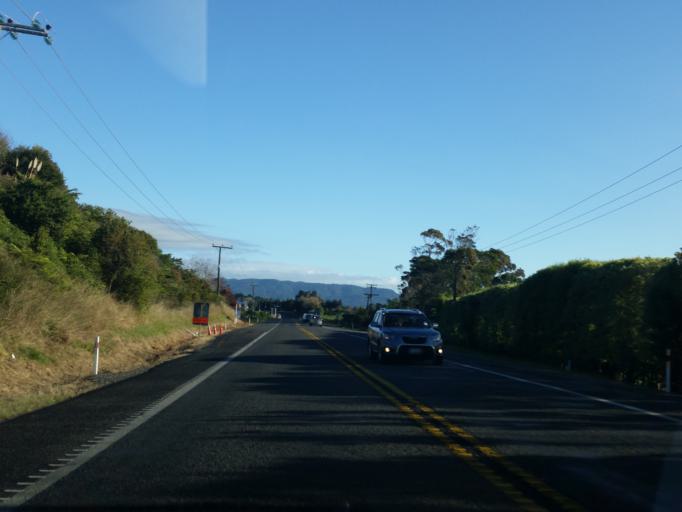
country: NZ
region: Bay of Plenty
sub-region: Western Bay of Plenty District
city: Katikati
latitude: -37.6086
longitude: 175.9437
